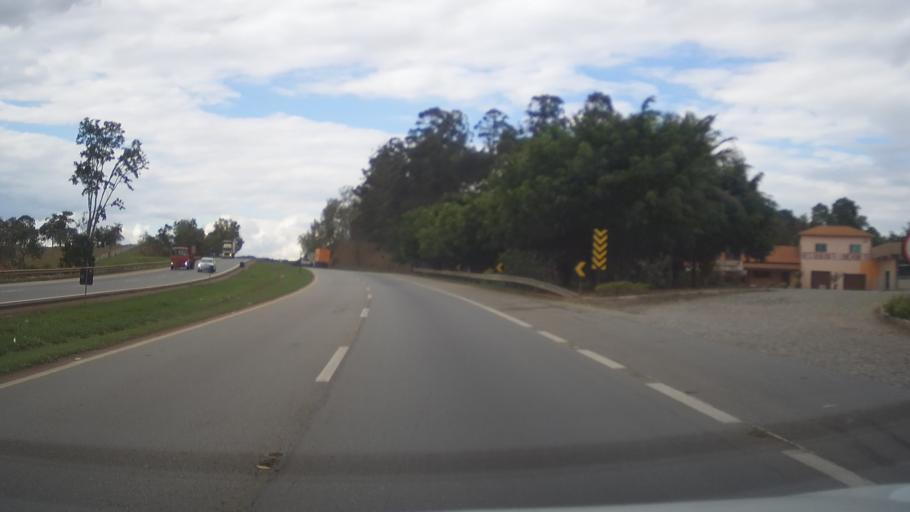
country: BR
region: Minas Gerais
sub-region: Itauna
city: Itauna
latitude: -20.2944
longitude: -44.4372
